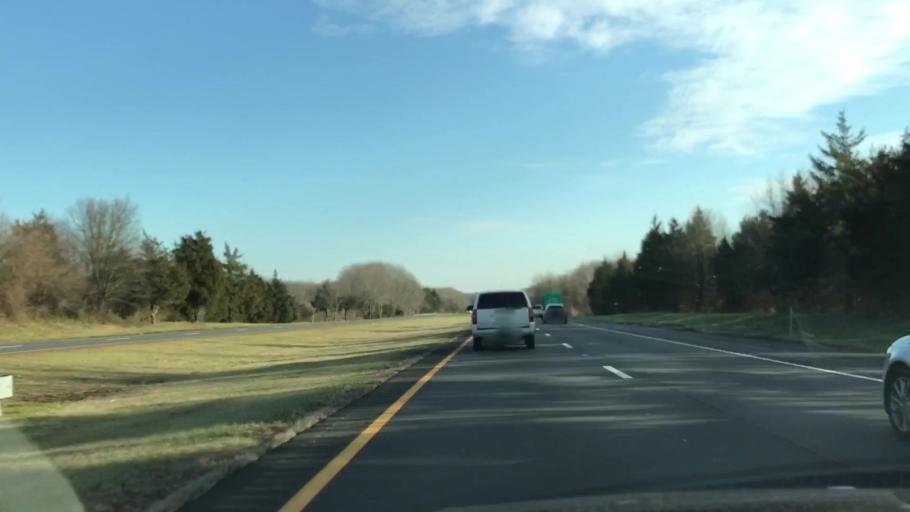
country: US
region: New Jersey
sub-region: Monmouth County
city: Shrewsbury
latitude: 40.1698
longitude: -74.4454
